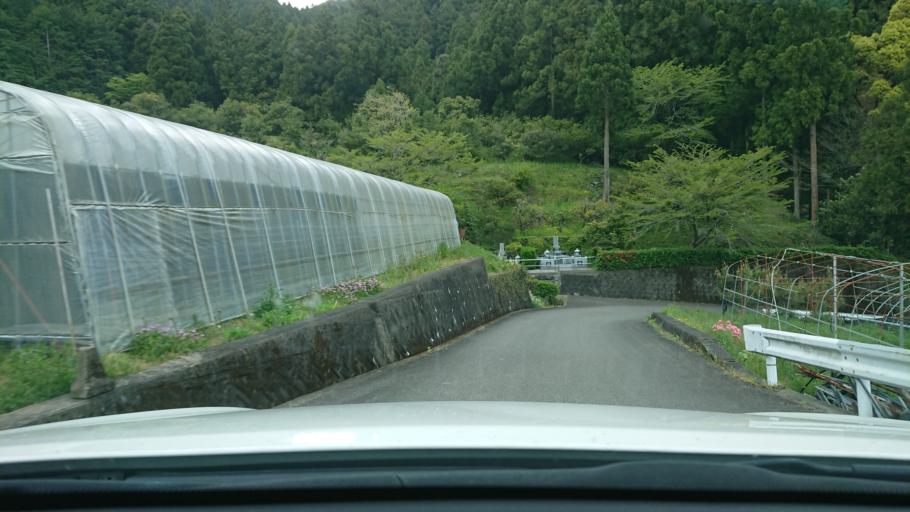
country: JP
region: Tokushima
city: Kamojimacho-jogejima
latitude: 33.8868
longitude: 134.3915
